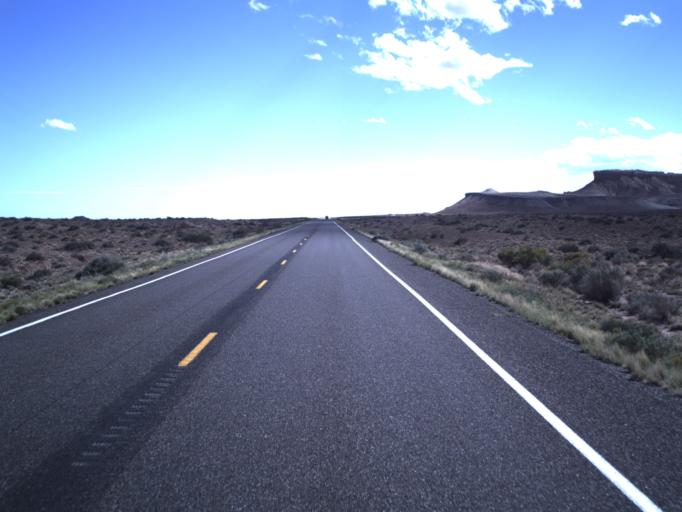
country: US
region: Utah
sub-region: Emery County
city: Ferron
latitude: 38.2965
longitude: -110.6676
